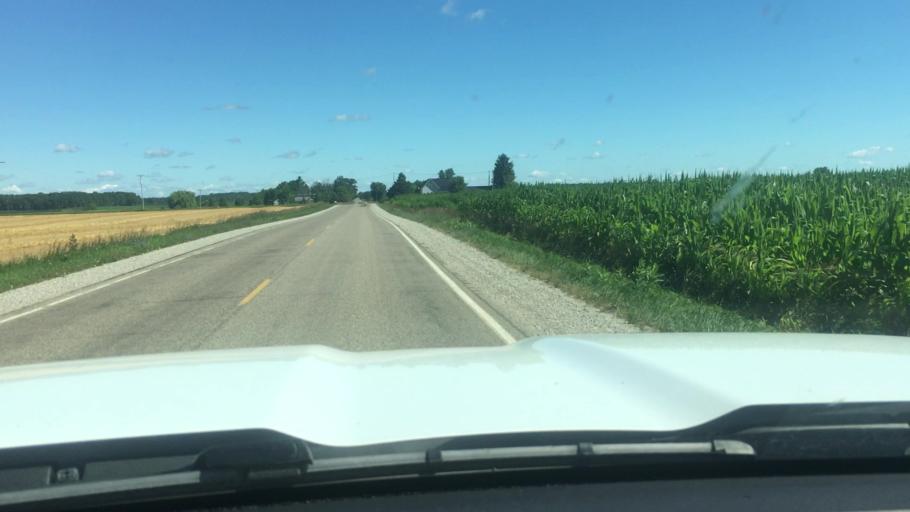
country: US
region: Michigan
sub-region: Montcalm County
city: Carson City
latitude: 43.2128
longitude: -84.7778
